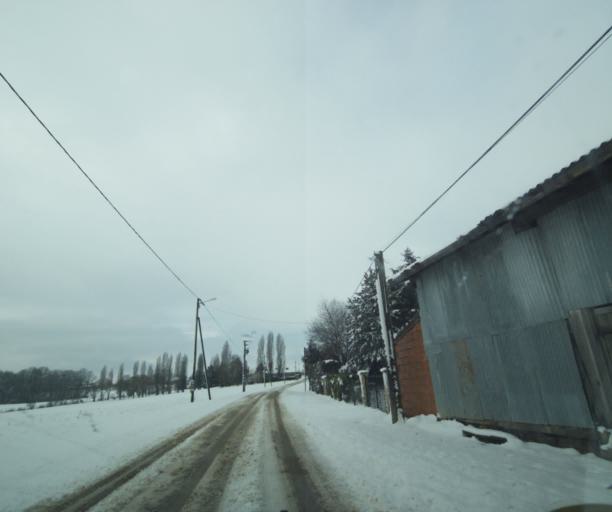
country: FR
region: Champagne-Ardenne
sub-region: Departement de la Haute-Marne
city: Montier-en-Der
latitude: 48.5248
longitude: 4.7145
